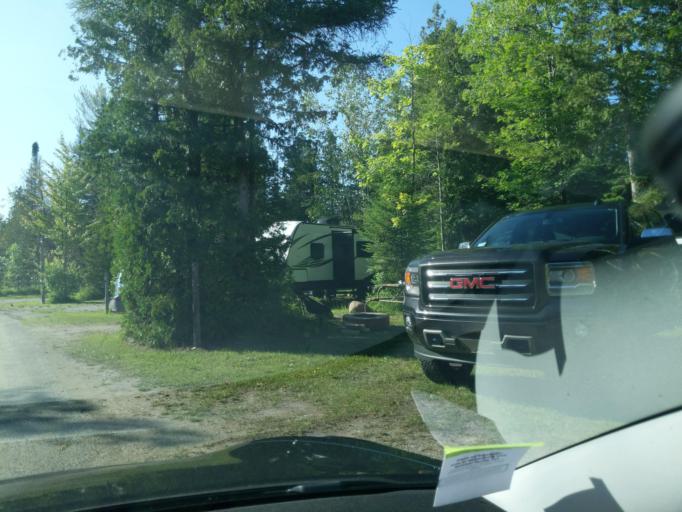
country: US
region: Michigan
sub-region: Mackinac County
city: Saint Ignace
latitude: 45.7502
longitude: -84.6815
